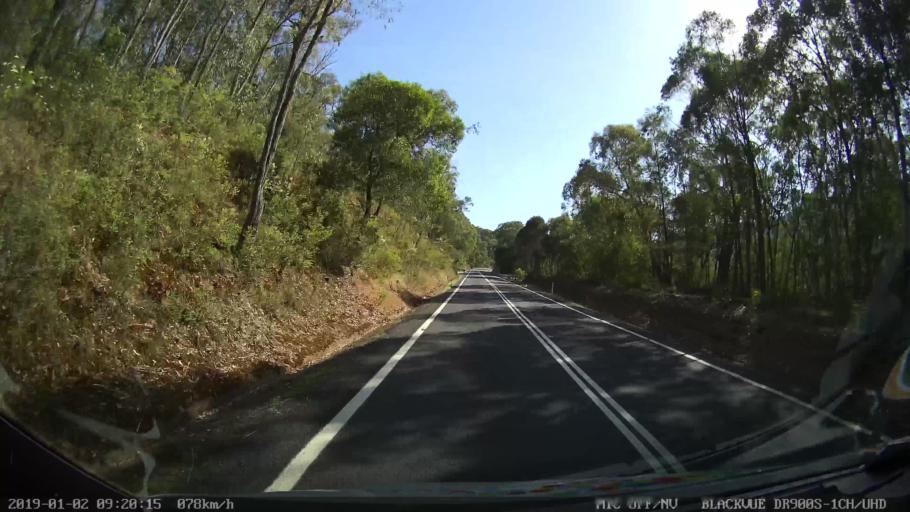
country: AU
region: New South Wales
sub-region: Tumut Shire
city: Tumut
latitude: -35.4138
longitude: 148.2818
